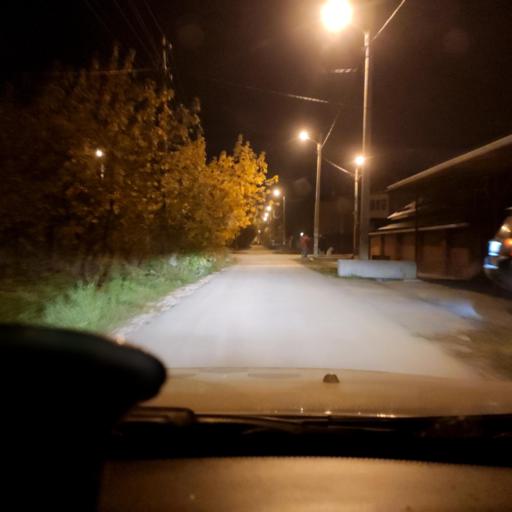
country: RU
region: Perm
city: Perm
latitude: 57.9813
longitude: 56.3005
